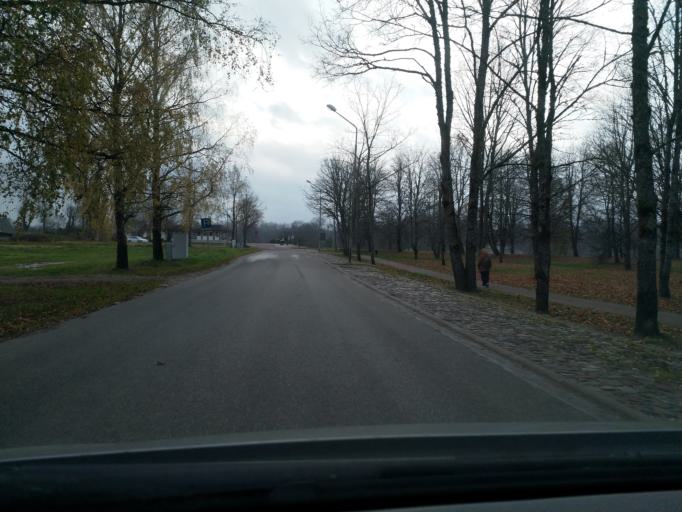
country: LV
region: Kuldigas Rajons
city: Kuldiga
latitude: 56.9718
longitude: 21.9794
